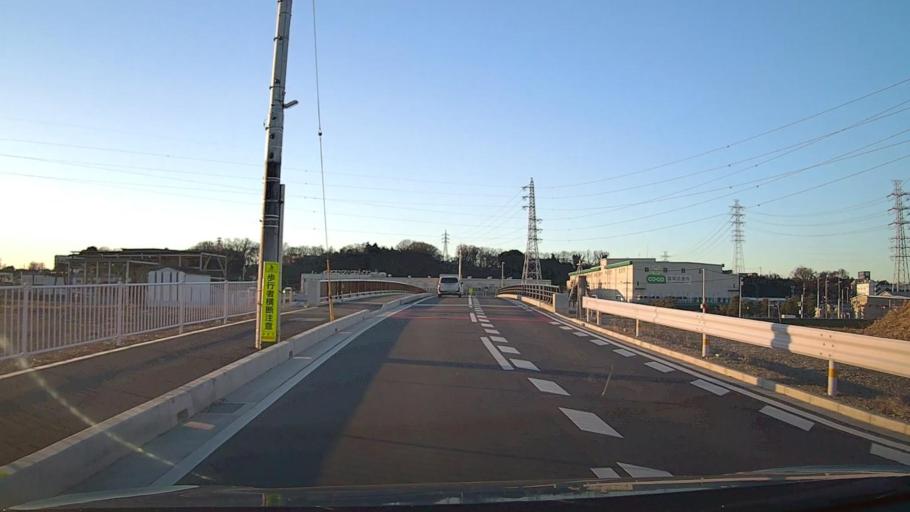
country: JP
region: Saitama
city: Shiki
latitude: 35.8074
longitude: 139.5432
